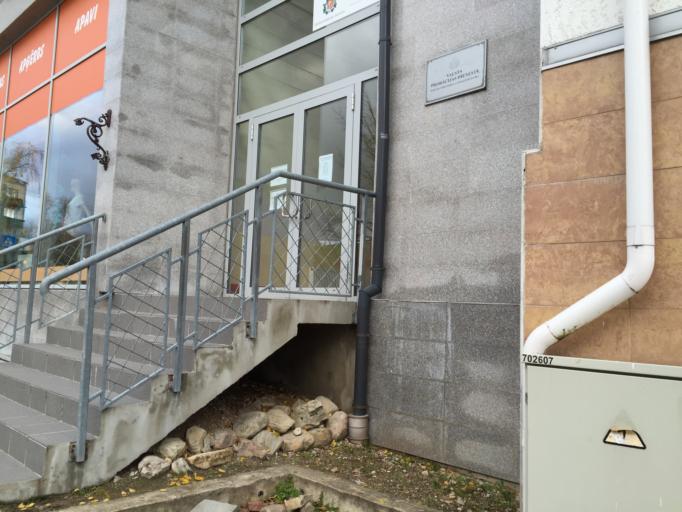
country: LV
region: Tukuma Rajons
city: Tukums
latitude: 56.9679
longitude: 23.1582
